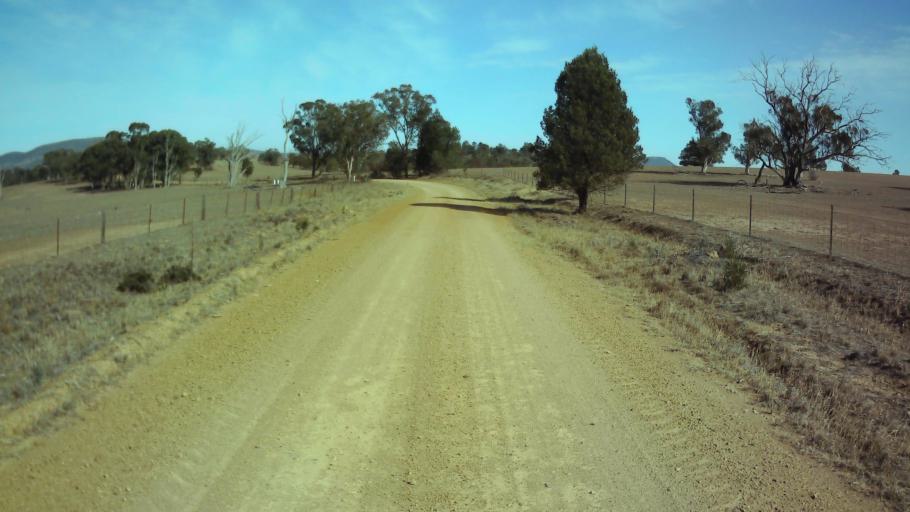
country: AU
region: New South Wales
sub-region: Weddin
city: Grenfell
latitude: -33.7549
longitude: 148.0244
